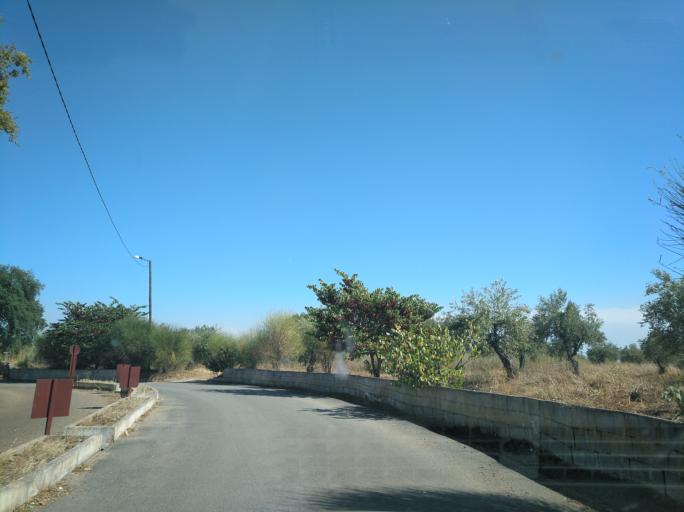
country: PT
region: Portalegre
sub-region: Elvas
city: Elvas
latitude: 38.9439
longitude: -7.2025
